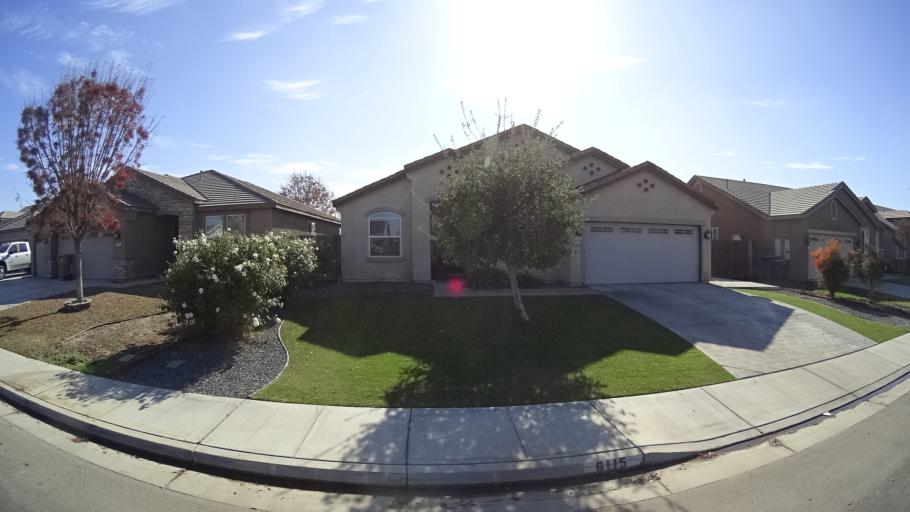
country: US
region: California
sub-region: Kern County
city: Greenfield
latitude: 35.2893
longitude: -119.0708
